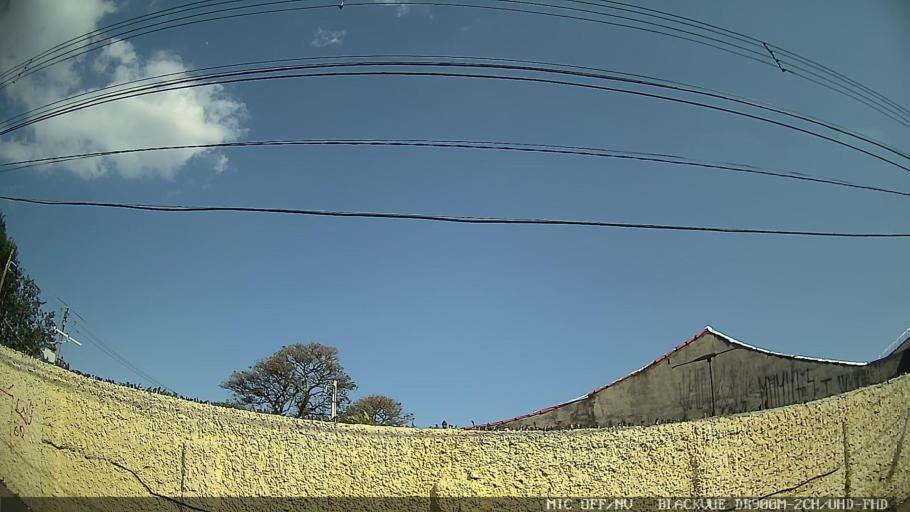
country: BR
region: Sao Paulo
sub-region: Ferraz De Vasconcelos
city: Ferraz de Vasconcelos
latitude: -23.5191
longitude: -46.4402
